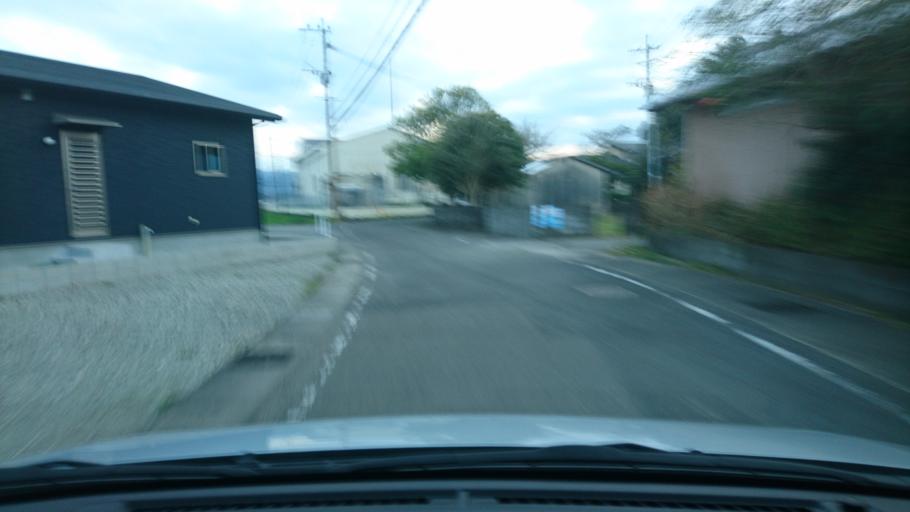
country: JP
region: Miyazaki
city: Miyazaki-shi
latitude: 31.8483
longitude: 131.4302
